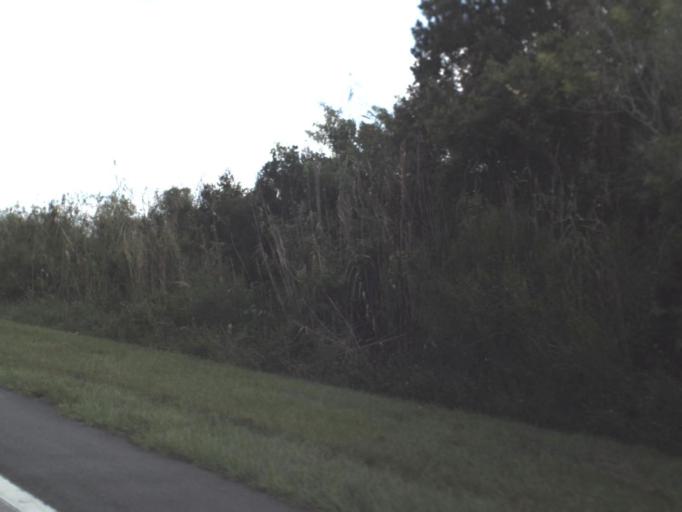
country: US
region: Florida
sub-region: Collier County
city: Marco
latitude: 25.8761
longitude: -81.2229
